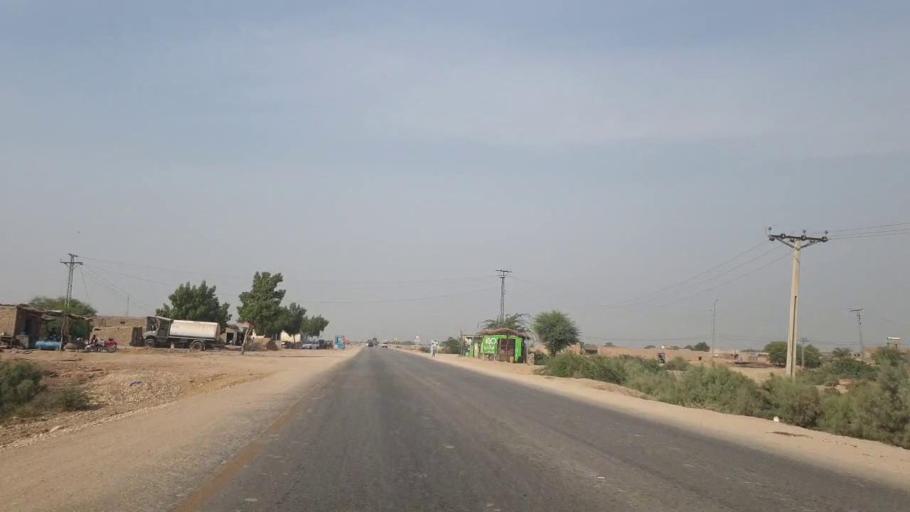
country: PK
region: Sindh
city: Sann
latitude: 26.0877
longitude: 68.0913
